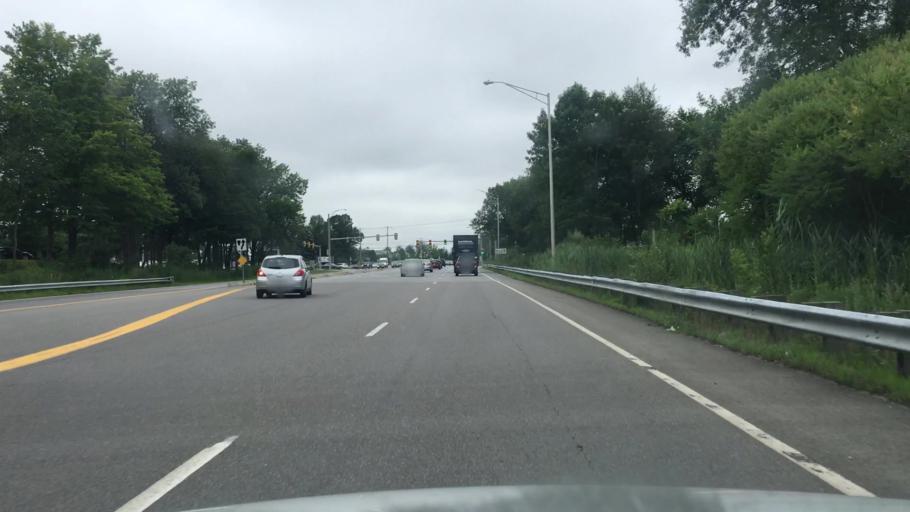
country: US
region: New Hampshire
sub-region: Rockingham County
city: Greenland
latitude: 43.0460
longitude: -70.8182
